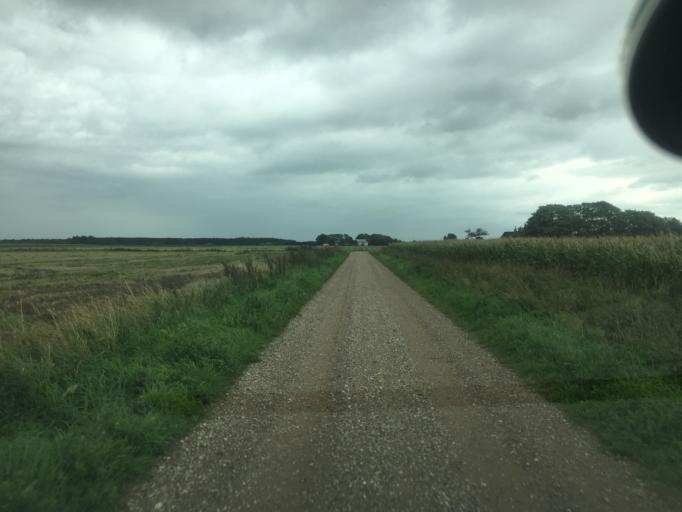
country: DK
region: South Denmark
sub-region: Tonder Kommune
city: Tonder
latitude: 54.9667
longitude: 8.9288
